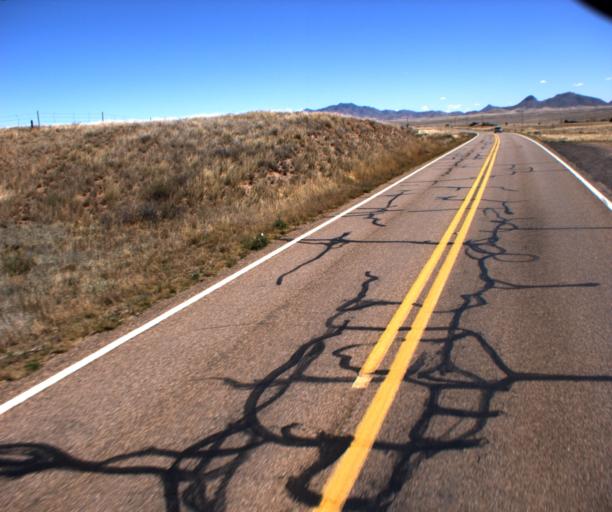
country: US
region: Arizona
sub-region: Cochise County
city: Huachuca City
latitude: 31.6830
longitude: -110.6274
